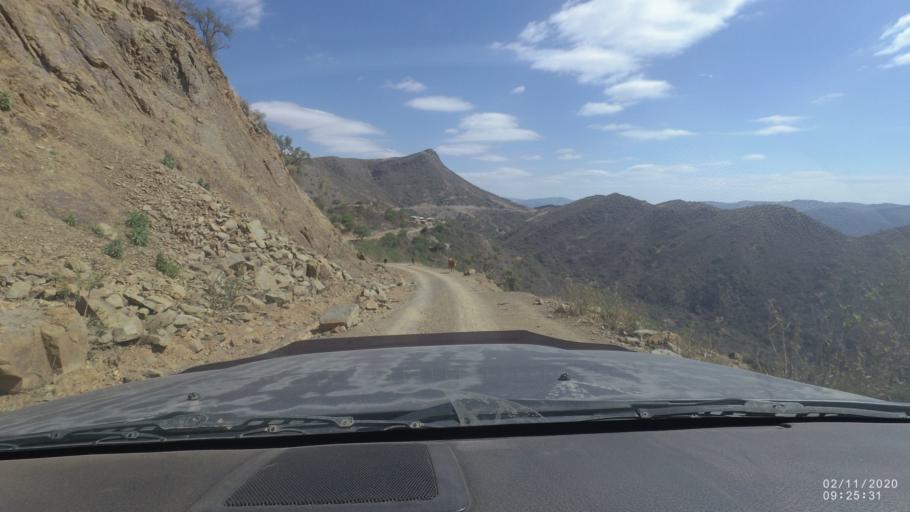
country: BO
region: Chuquisaca
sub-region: Provincia Zudanez
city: Mojocoya
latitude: -18.4542
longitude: -64.5829
